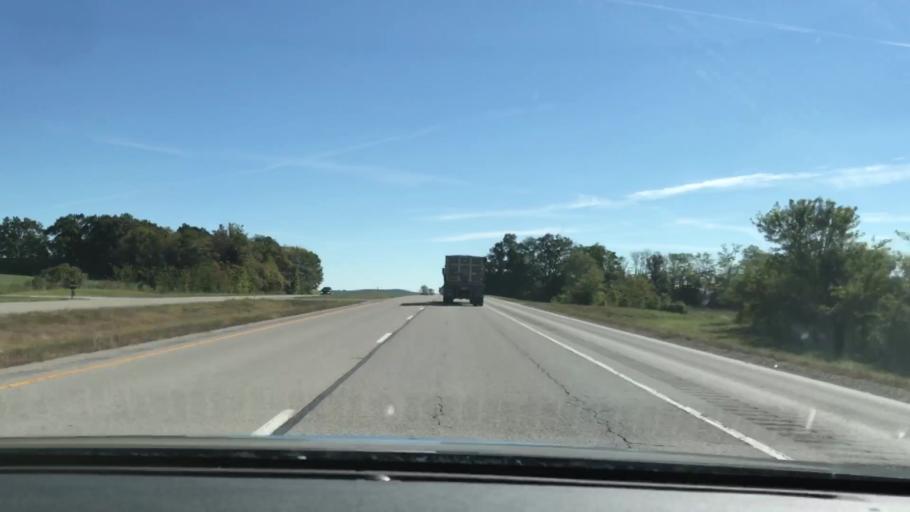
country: US
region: Kentucky
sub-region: Todd County
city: Elkton
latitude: 36.8462
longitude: -87.2939
